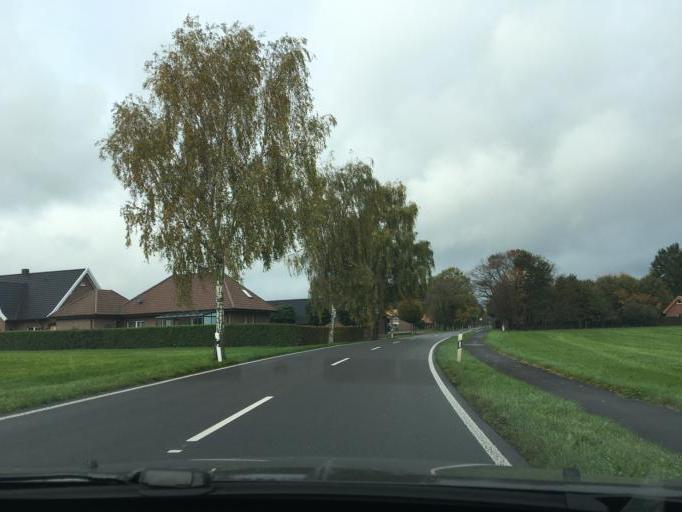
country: DE
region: North Rhine-Westphalia
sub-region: Regierungsbezirk Munster
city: Vreden
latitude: 52.0603
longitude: 6.7976
